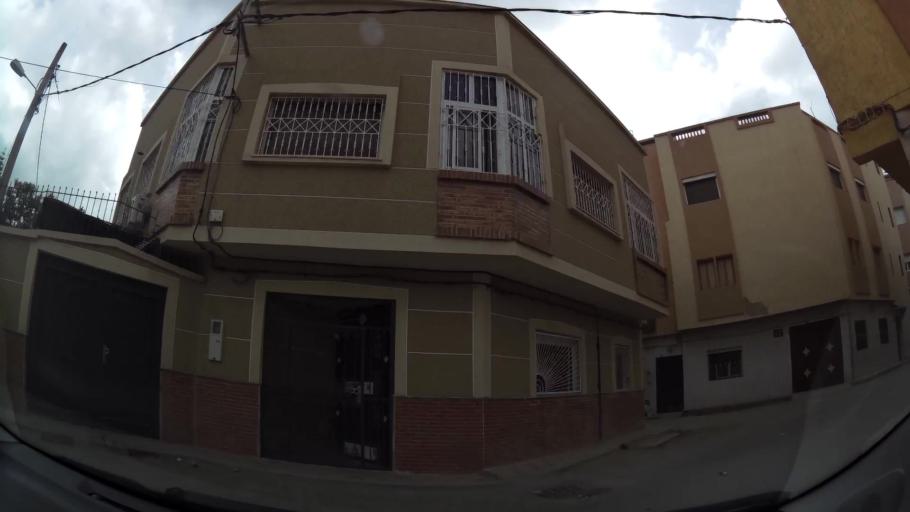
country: MA
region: Oriental
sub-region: Nador
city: Nador
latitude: 35.1638
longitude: -2.9331
